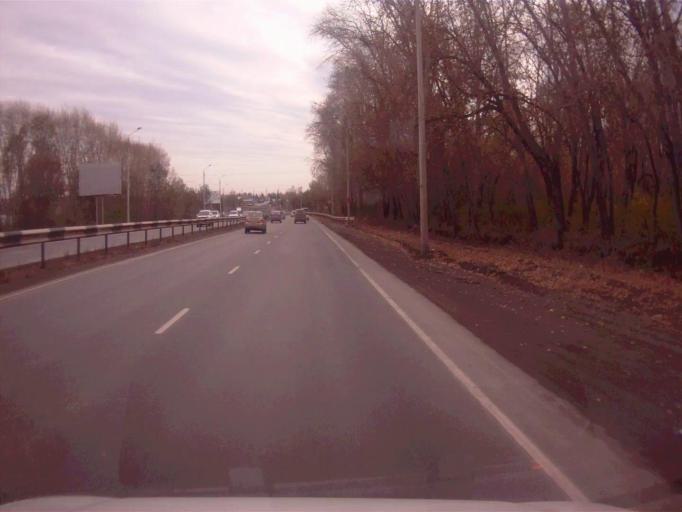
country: RU
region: Chelyabinsk
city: Novosineglazovskiy
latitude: 55.0496
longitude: 61.4138
